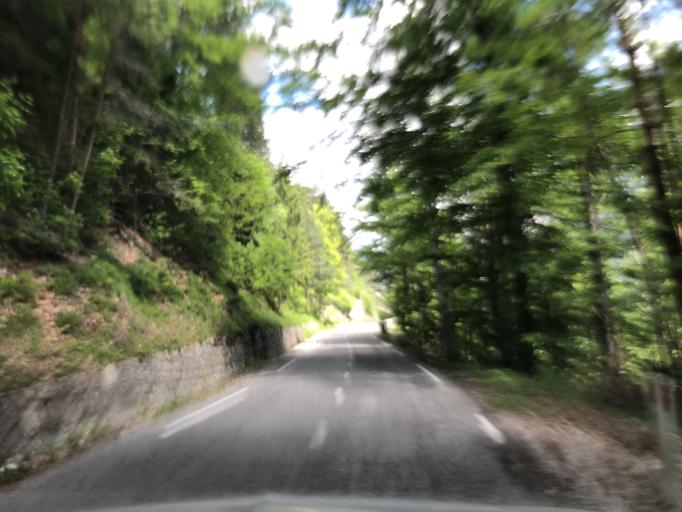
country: SI
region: Bovec
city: Bovec
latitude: 46.4120
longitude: 13.6113
